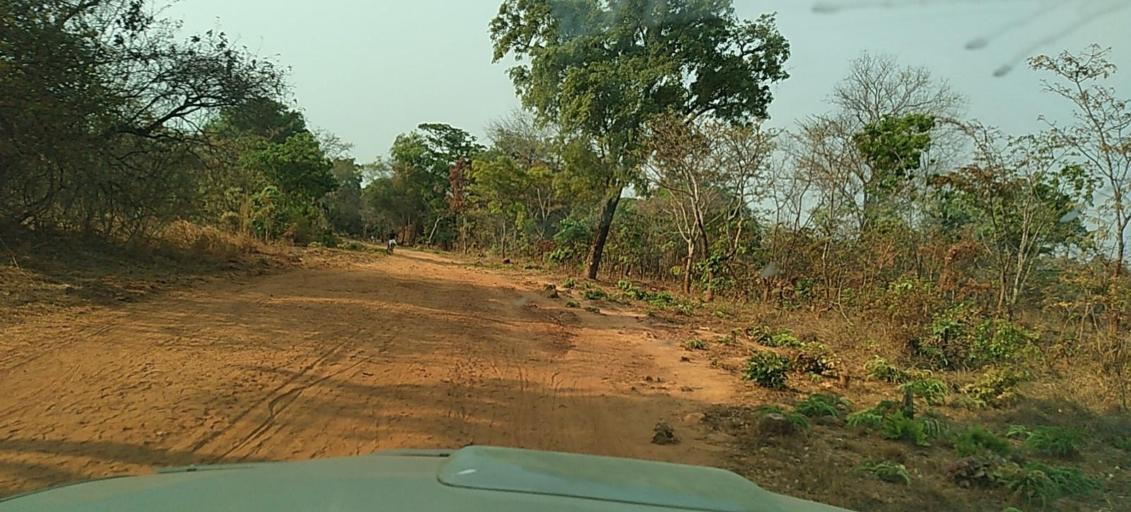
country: ZM
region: North-Western
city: Kasempa
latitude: -13.2916
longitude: 26.5551
